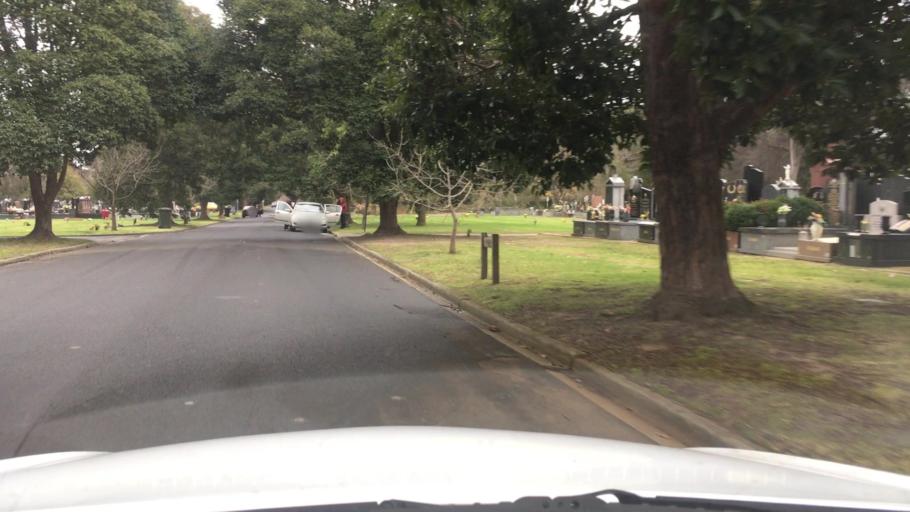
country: AU
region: Victoria
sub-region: Greater Dandenong
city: Noble Park North
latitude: -37.9404
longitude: 145.1843
